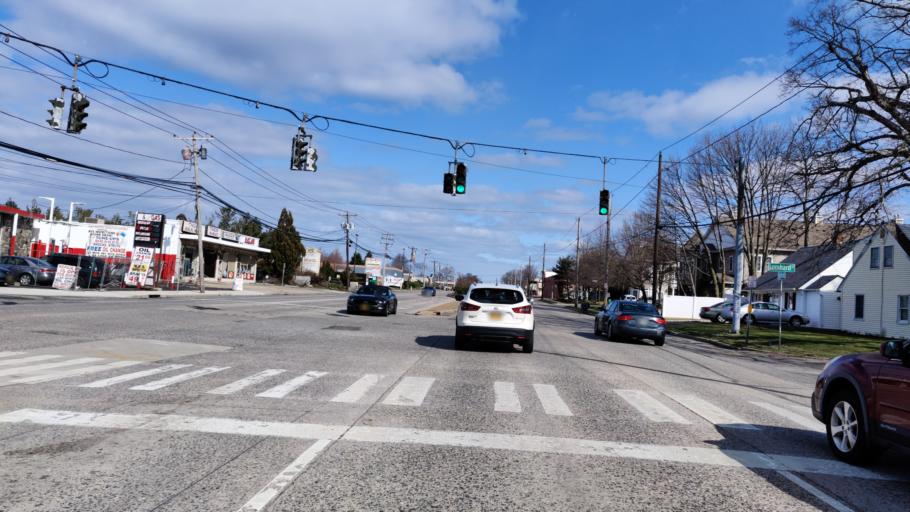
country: US
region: New York
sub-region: Suffolk County
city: Deer Park
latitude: 40.7471
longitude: -73.3235
